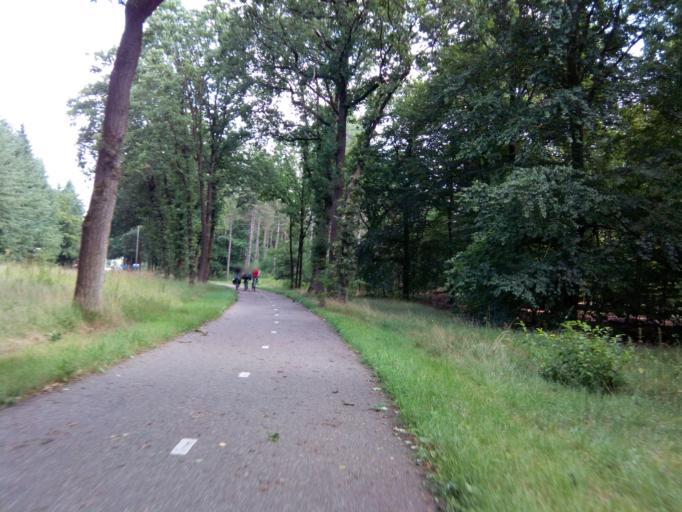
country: NL
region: Utrecht
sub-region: Gemeente Utrechtse Heuvelrug
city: Maarn
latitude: 52.0875
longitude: 5.3617
